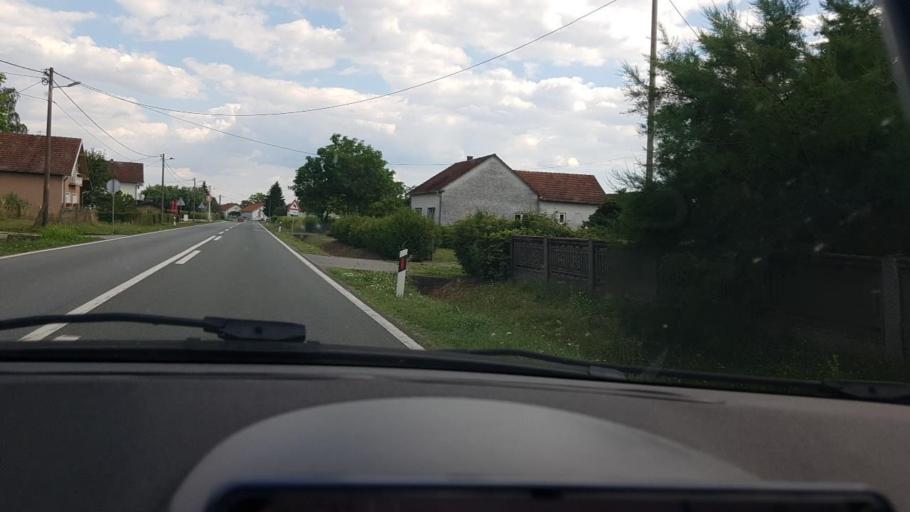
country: HR
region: Bjelovarsko-Bilogorska
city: Zdralovi
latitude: 45.8584
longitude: 16.9231
